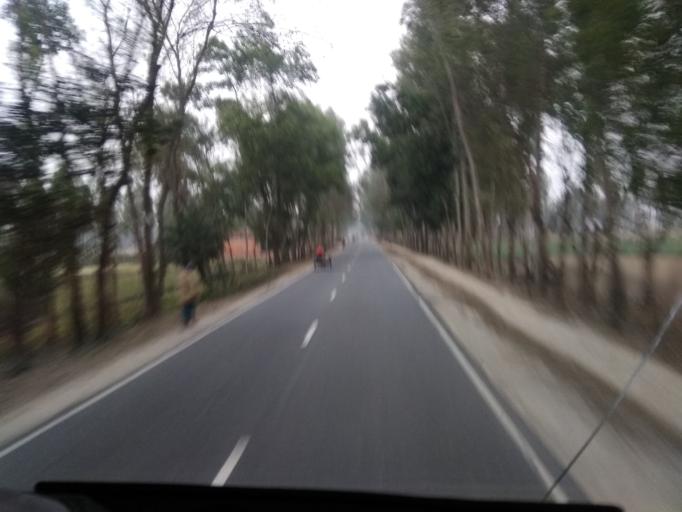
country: BD
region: Rajshahi
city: Bogra
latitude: 24.6754
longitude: 89.2823
